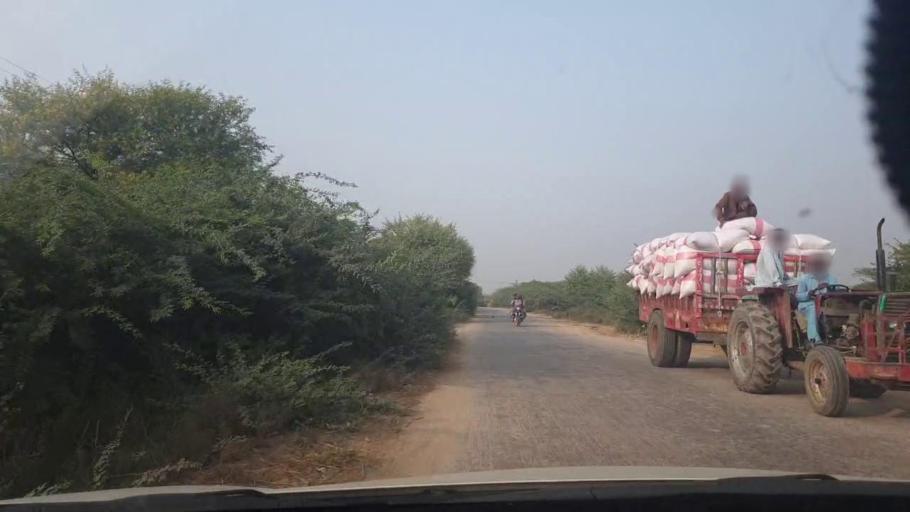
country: PK
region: Sindh
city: Bulri
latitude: 24.7673
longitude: 68.4206
